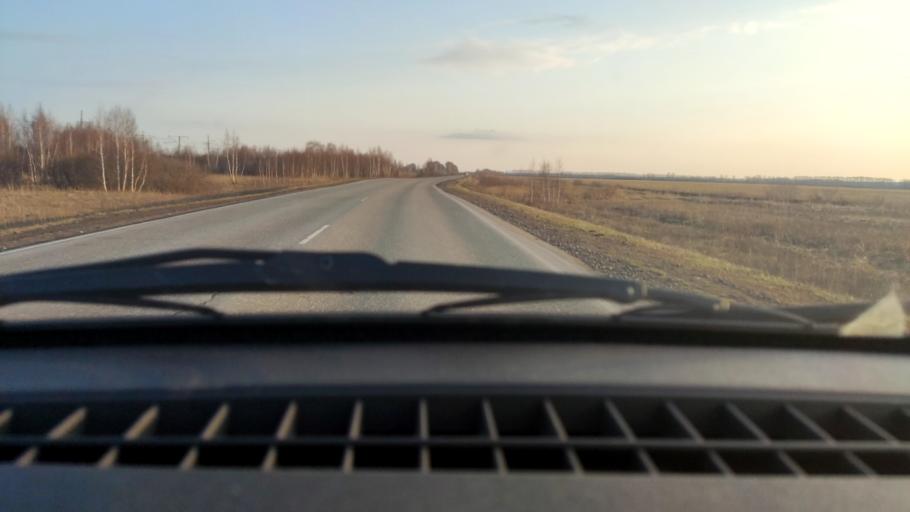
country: RU
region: Bashkortostan
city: Chishmy
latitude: 54.4290
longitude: 55.2337
